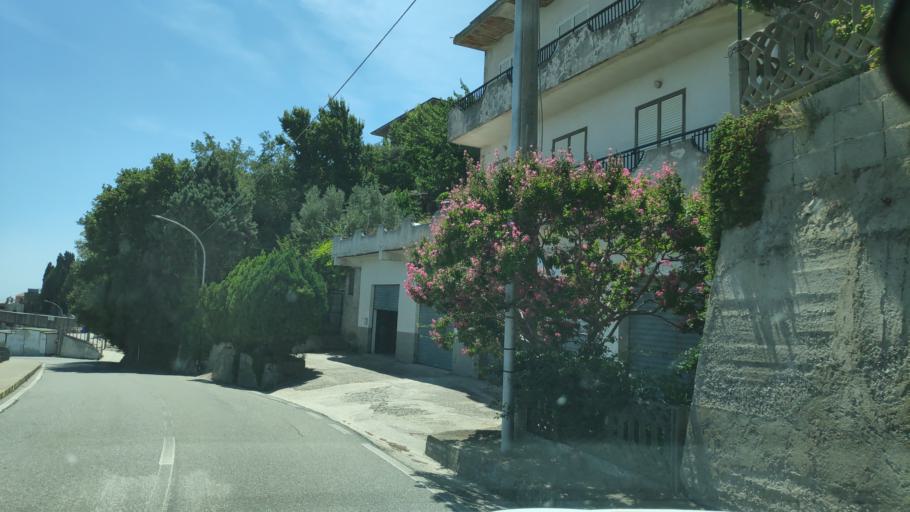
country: IT
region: Calabria
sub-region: Provincia di Catanzaro
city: Gasperina
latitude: 38.7376
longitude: 16.5123
